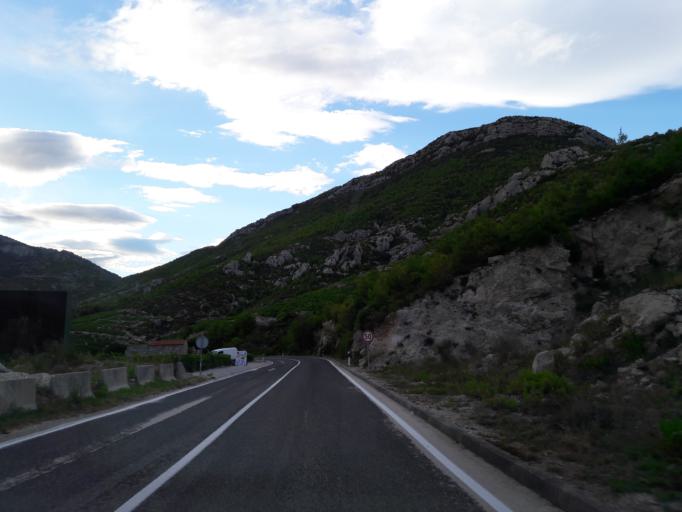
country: HR
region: Dubrovacko-Neretvanska
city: Ston
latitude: 42.8219
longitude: 17.6728
